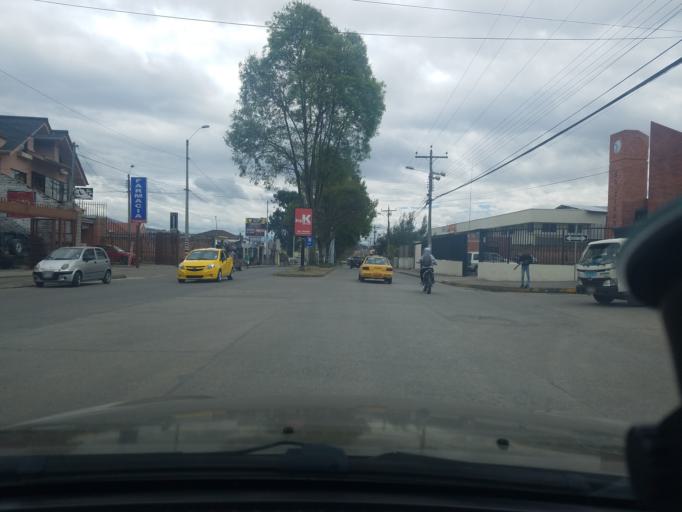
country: EC
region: Azuay
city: Cuenca
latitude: -2.9161
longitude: -79.0332
